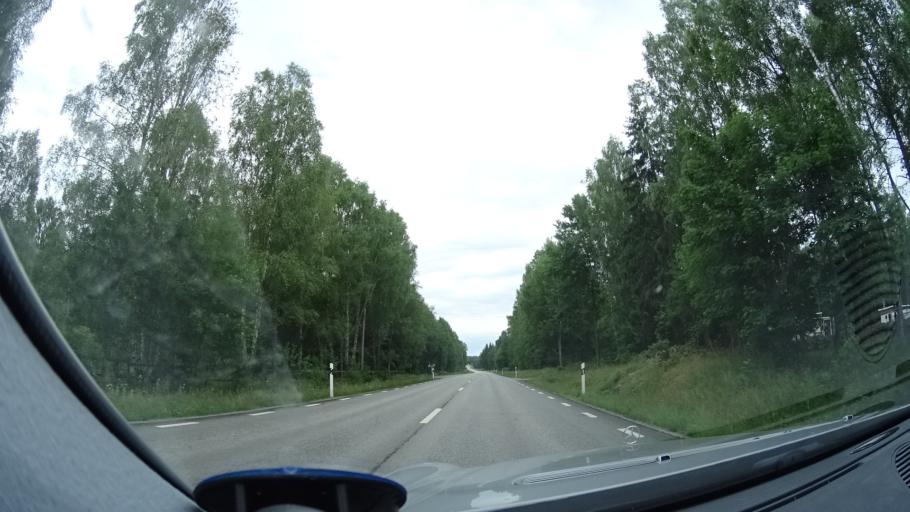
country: SE
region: Kronoberg
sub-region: Tingsryds Kommun
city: Tingsryd
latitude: 56.4817
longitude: 15.0031
